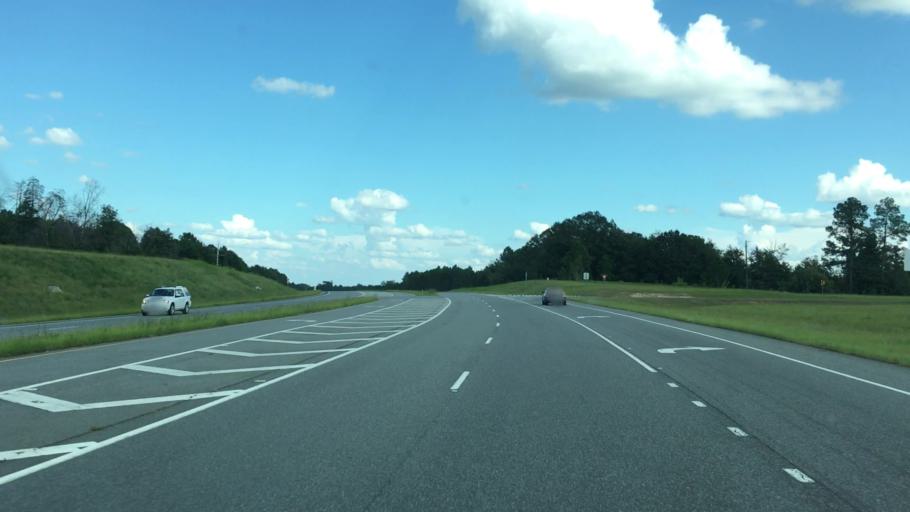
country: US
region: Georgia
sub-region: Laurens County
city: Dublin
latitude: 32.5023
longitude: -82.9404
